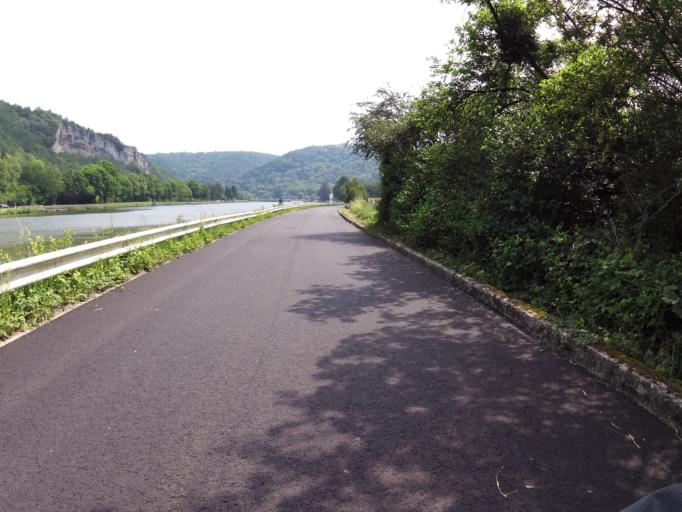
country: BE
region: Wallonia
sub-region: Province de Namur
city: Hastiere-Lavaux
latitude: 50.2084
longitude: 4.8484
